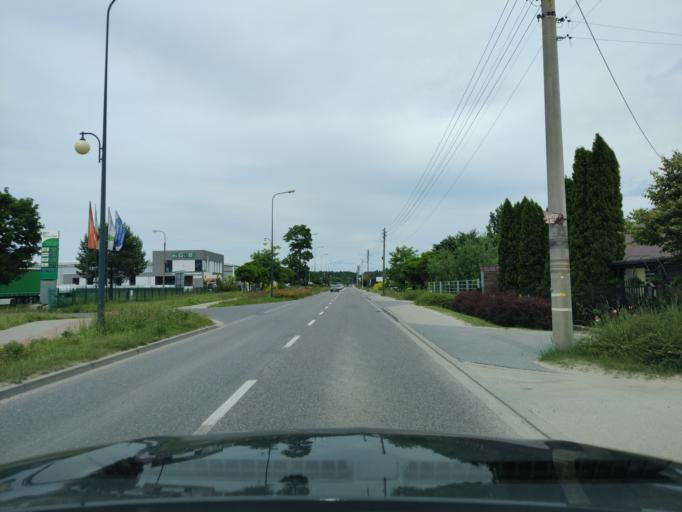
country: PL
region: Masovian Voivodeship
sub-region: Powiat wyszkowski
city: Wyszkow
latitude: 52.6132
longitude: 21.4535
